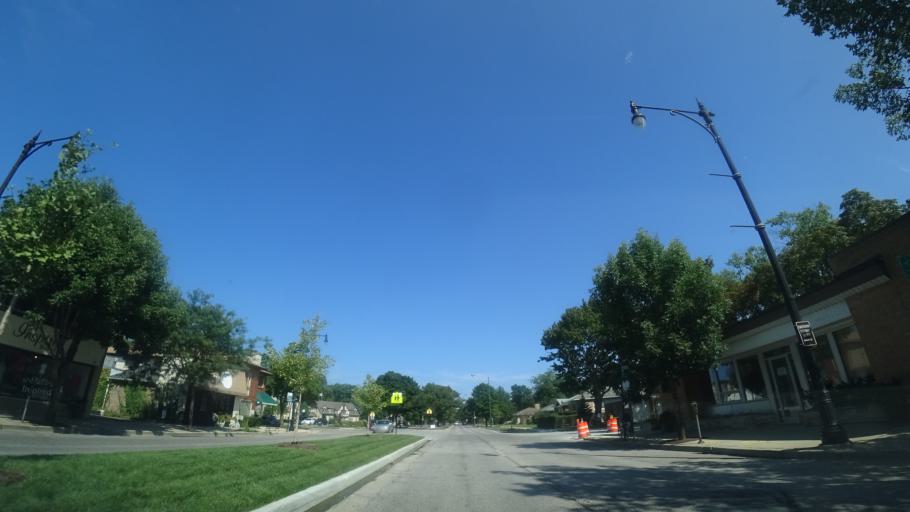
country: US
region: Illinois
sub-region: Cook County
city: Lincolnwood
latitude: 41.9958
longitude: -87.7621
